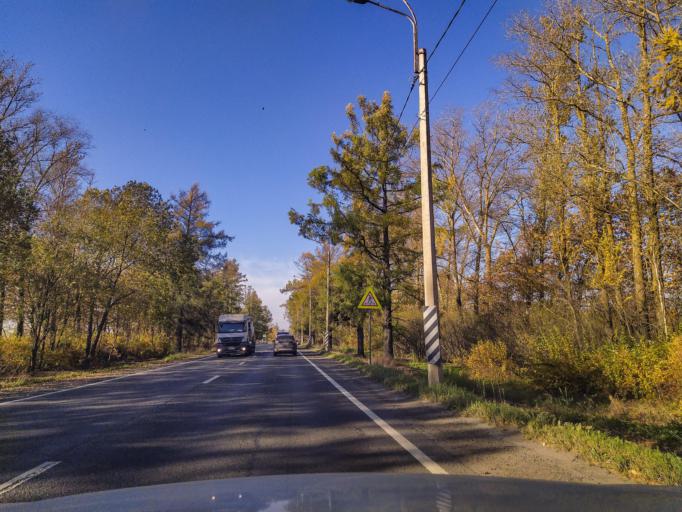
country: RU
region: St.-Petersburg
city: Aleksandrovskaya
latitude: 59.7067
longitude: 30.3356
